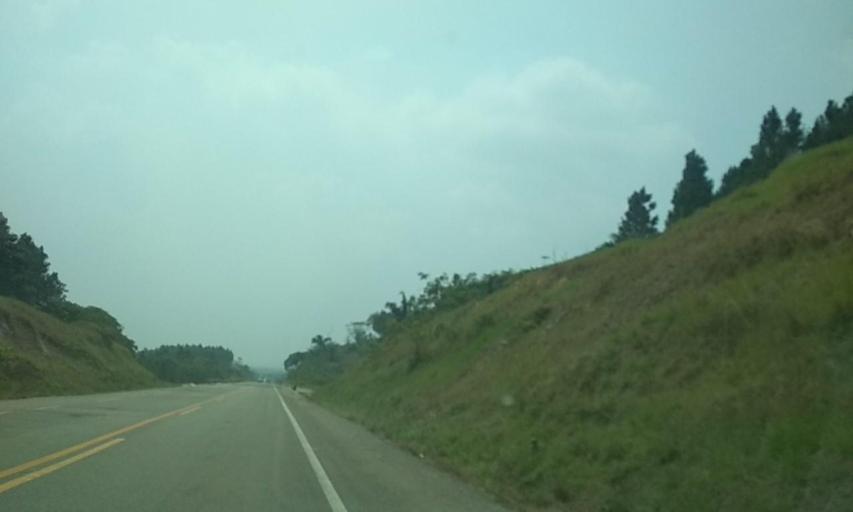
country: MX
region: Tabasco
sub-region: Huimanguillo
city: Francisco Rueda
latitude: 17.7500
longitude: -93.9943
